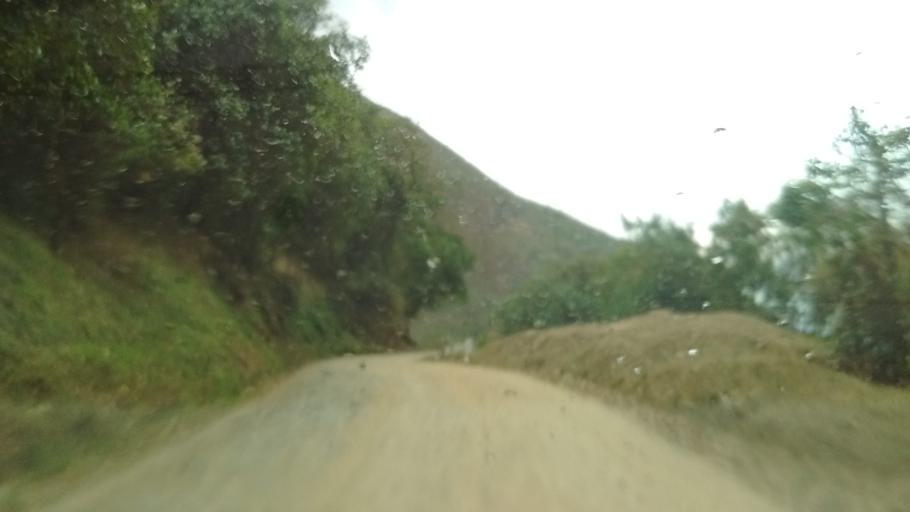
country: CO
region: Cauca
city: La Vega
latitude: 2.0344
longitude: -76.7954
